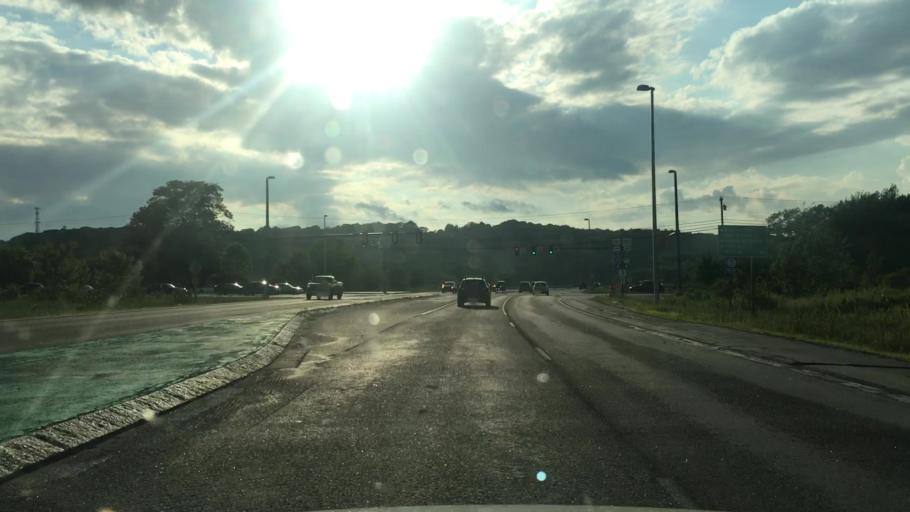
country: US
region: Maine
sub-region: Kennebec County
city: Augusta
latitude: 44.3331
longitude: -69.7598
